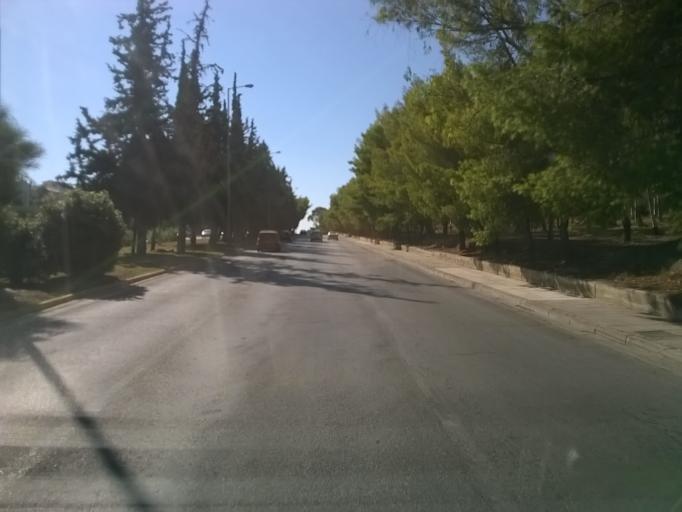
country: GR
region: Attica
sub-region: Nomarchia Anatolikis Attikis
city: Vouliagmeni
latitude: 37.8243
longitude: 23.7746
